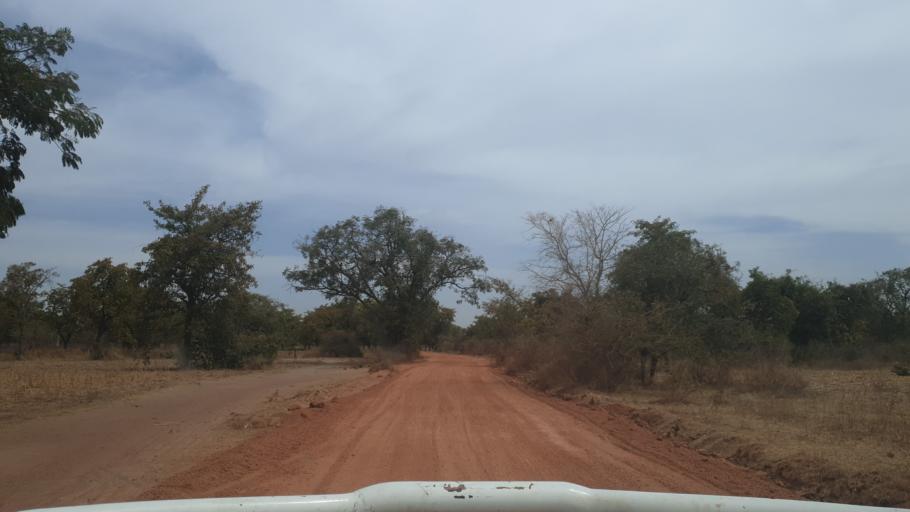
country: ML
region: Sikasso
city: Yorosso
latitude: 12.2256
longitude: -4.7516
